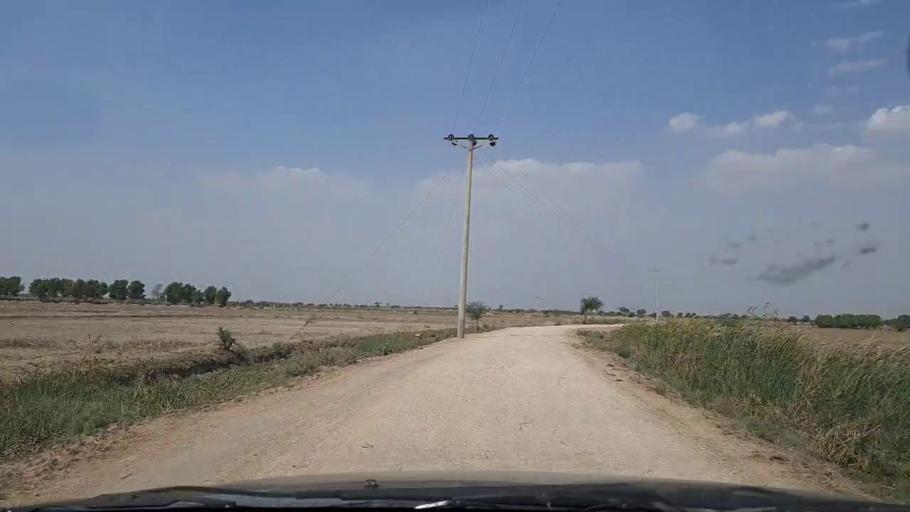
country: PK
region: Sindh
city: Mirpur Batoro
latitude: 24.6202
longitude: 68.2380
